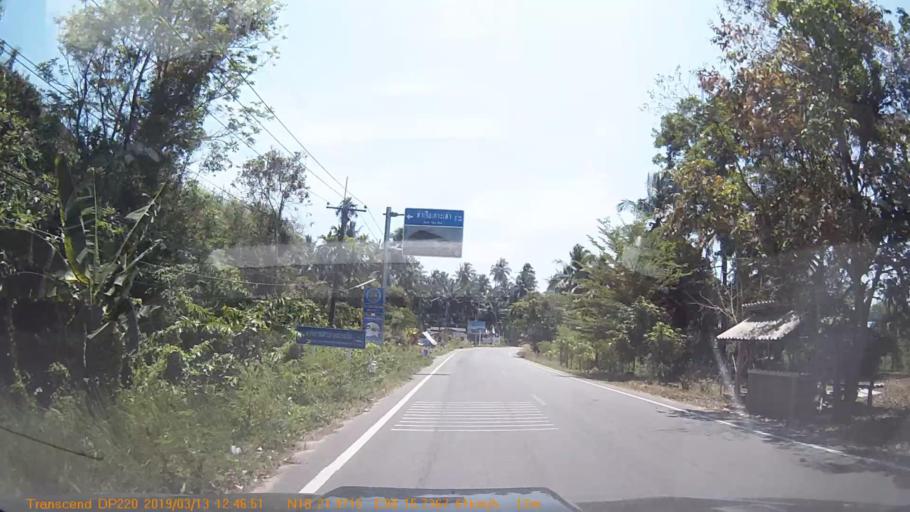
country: TH
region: Chumphon
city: Chumphon
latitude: 10.3658
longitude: 99.2622
